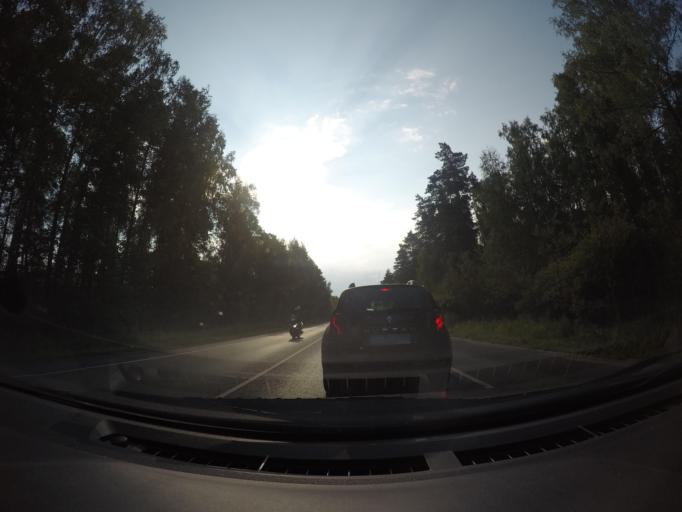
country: RU
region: Moskovskaya
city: Ramenskoye
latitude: 55.6380
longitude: 38.2515
